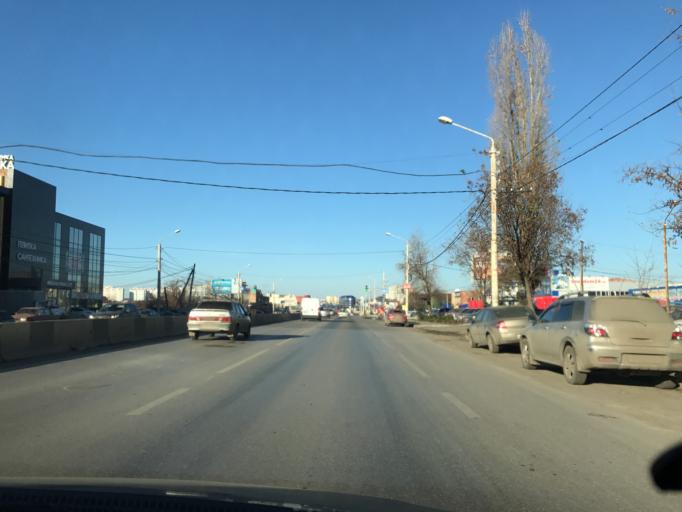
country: RU
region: Rostov
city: Kalinin
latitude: 47.2159
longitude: 39.6135
